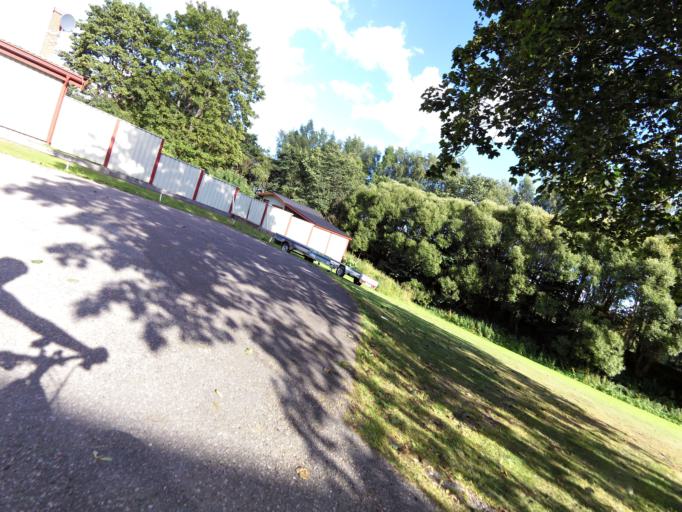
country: SE
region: Gaevleborg
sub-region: Gavle Kommun
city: Gavle
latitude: 60.6939
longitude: 17.1595
